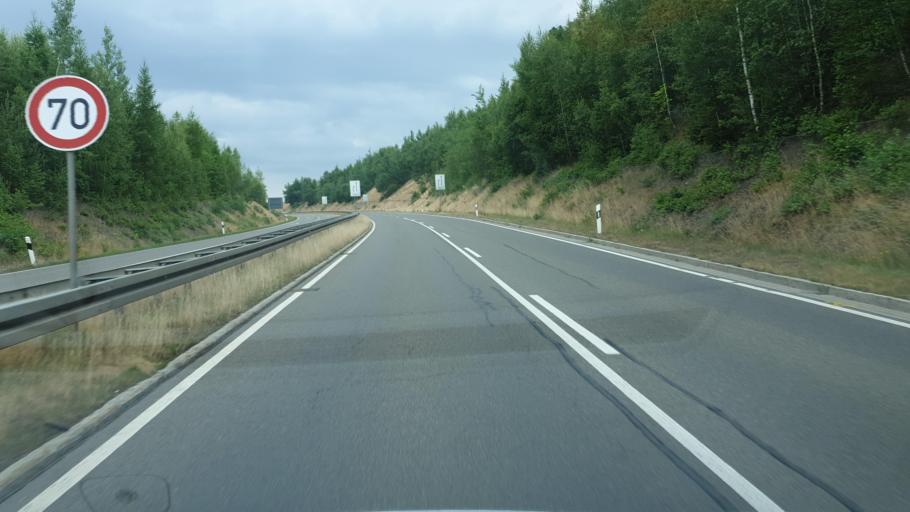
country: DE
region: Saxony
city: Reichenbach/Vogtland
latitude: 50.6071
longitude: 12.3161
